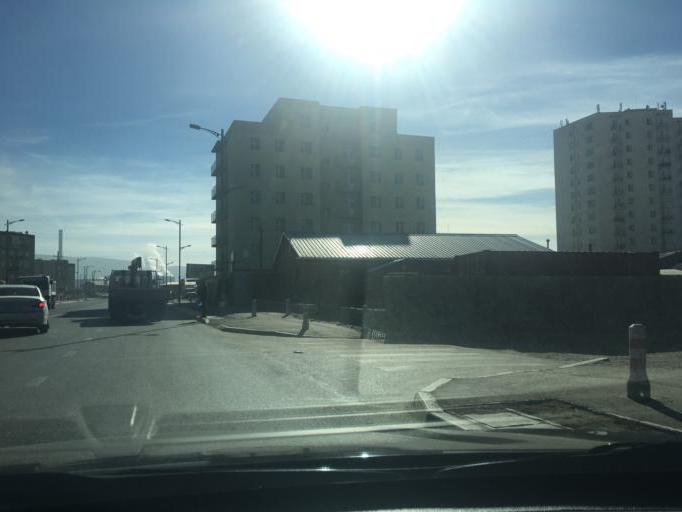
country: MN
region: Ulaanbaatar
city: Ulaanbaatar
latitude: 47.9124
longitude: 106.7829
